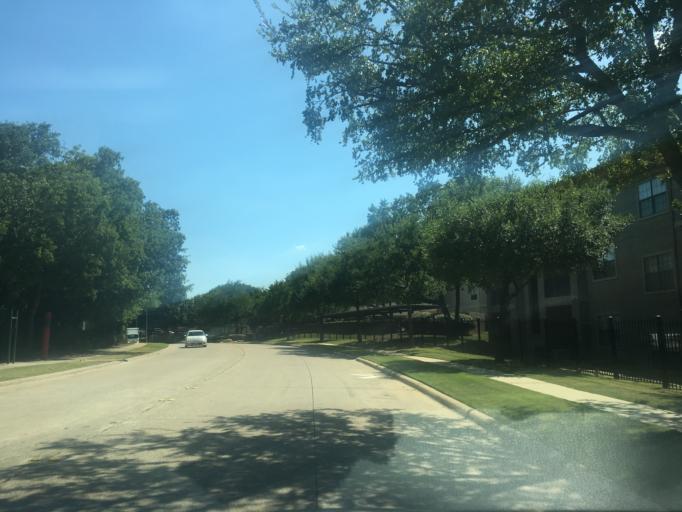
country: US
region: Texas
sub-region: Denton County
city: Lewisville
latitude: 33.0083
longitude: -96.9894
